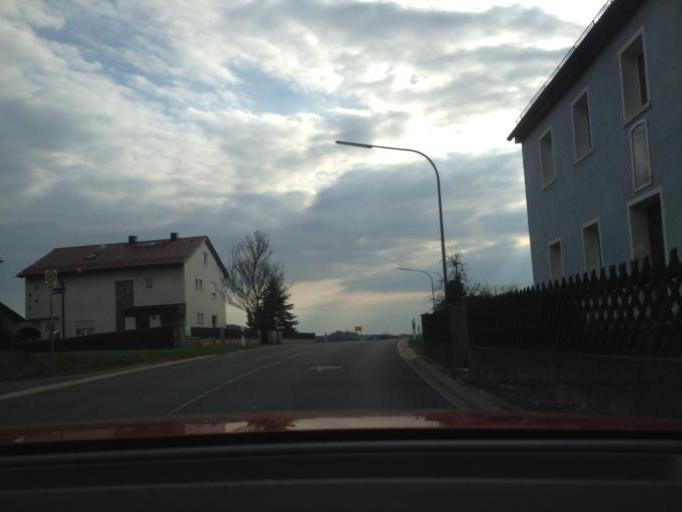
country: DE
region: Bavaria
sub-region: Upper Palatinate
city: Kemnath
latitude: 49.8535
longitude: 11.8667
